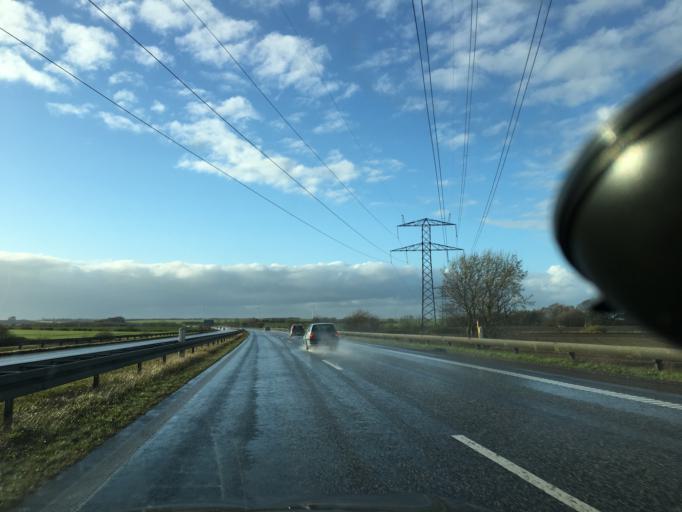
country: DK
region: Central Jutland
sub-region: Randers Kommune
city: Spentrup
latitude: 56.5028
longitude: 9.9763
